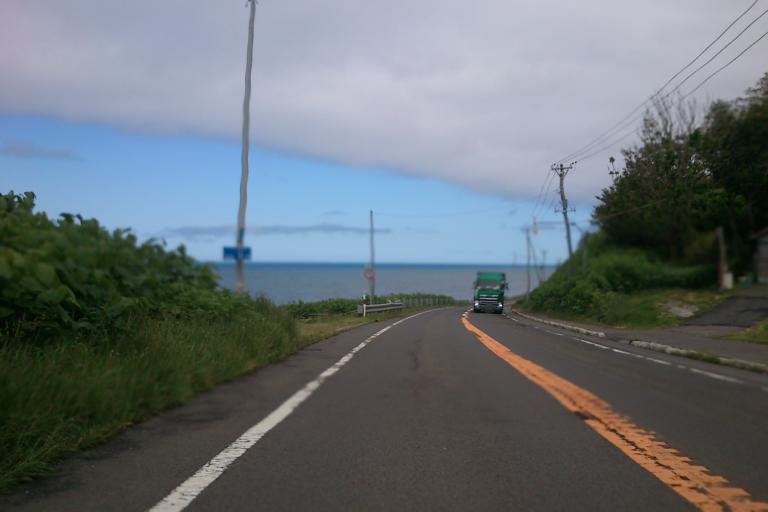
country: JP
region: Hokkaido
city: Ishikari
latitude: 43.4234
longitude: 141.4269
